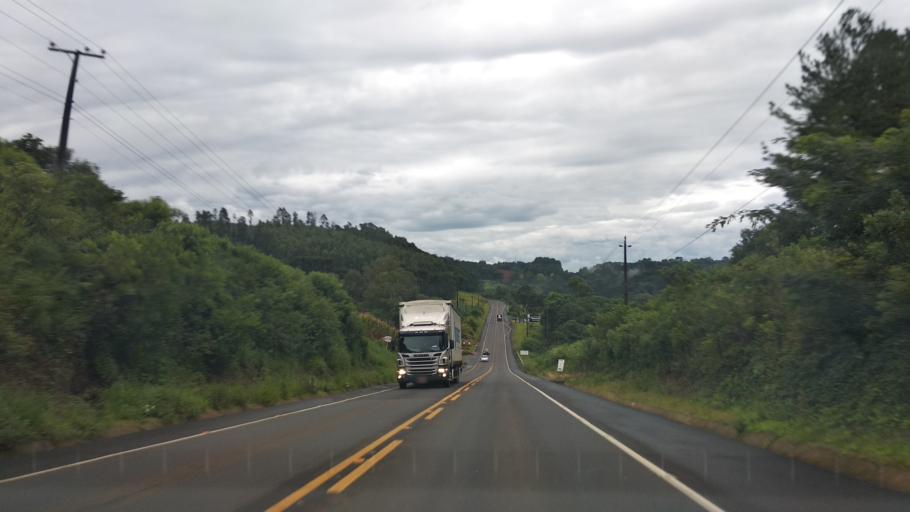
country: BR
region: Santa Catarina
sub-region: Videira
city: Videira
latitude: -27.0472
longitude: -51.1648
